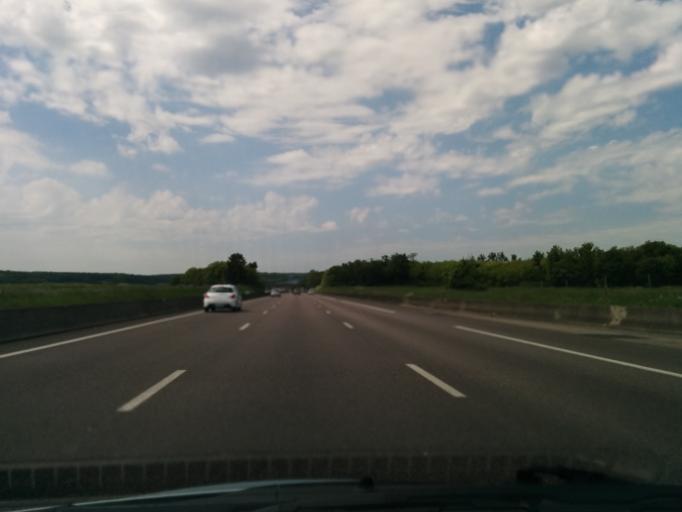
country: FR
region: Ile-de-France
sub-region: Departement des Yvelines
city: Buchelay
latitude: 48.9878
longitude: 1.6605
